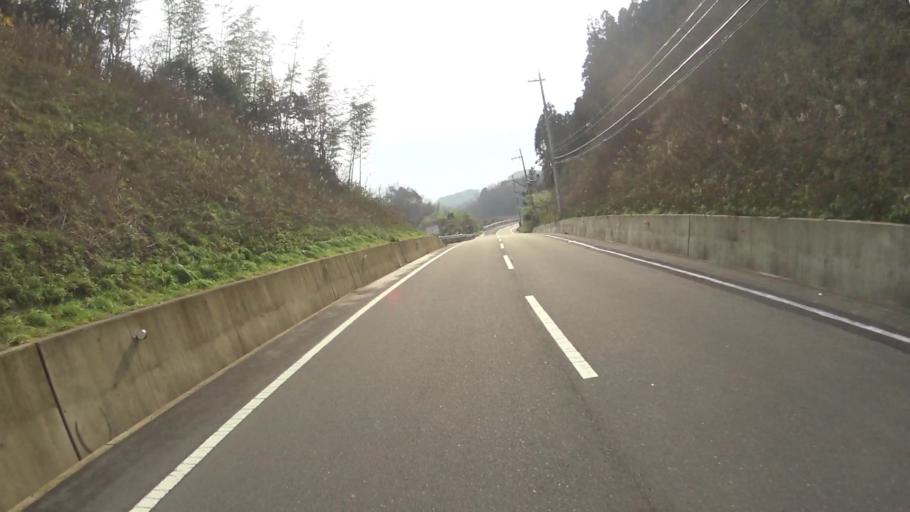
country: JP
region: Kyoto
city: Maizuru
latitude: 35.4847
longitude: 135.3240
